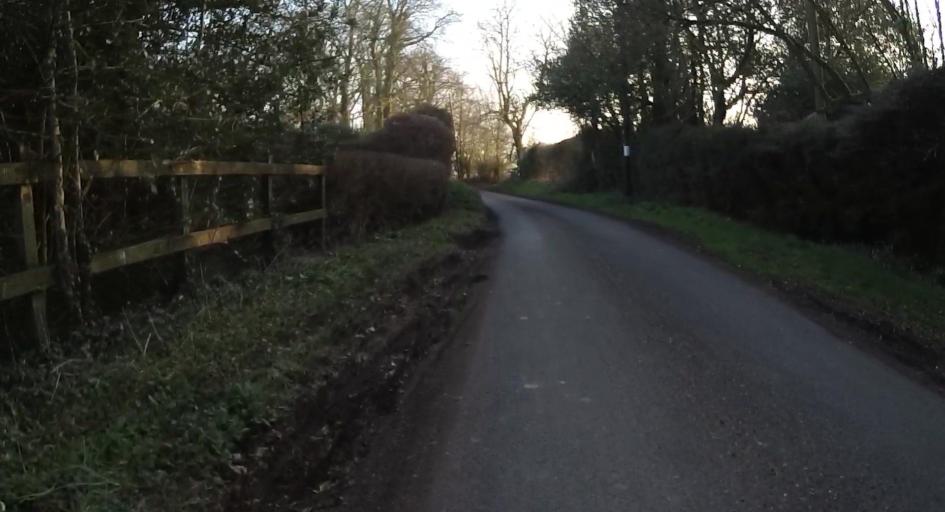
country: GB
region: England
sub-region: Hampshire
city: Alton
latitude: 51.1683
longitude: -1.0019
